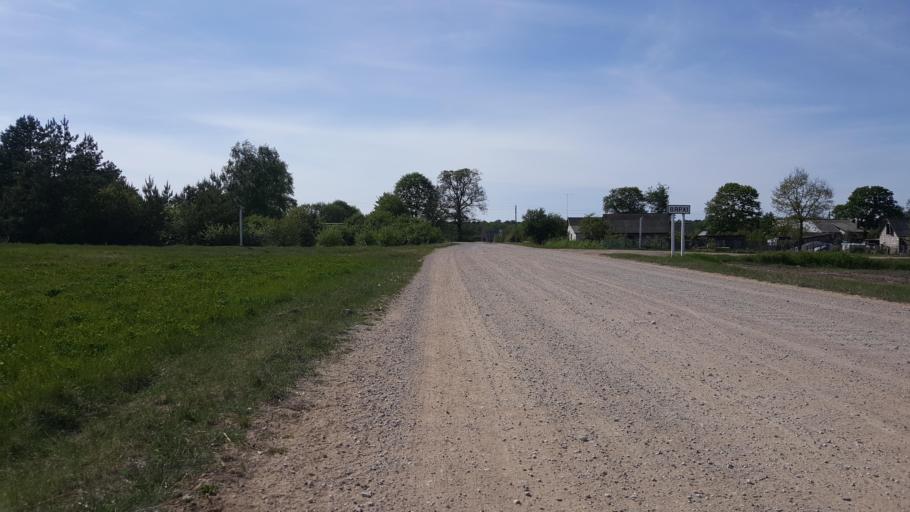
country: BY
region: Brest
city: Zhabinka
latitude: 52.3151
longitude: 24.0430
